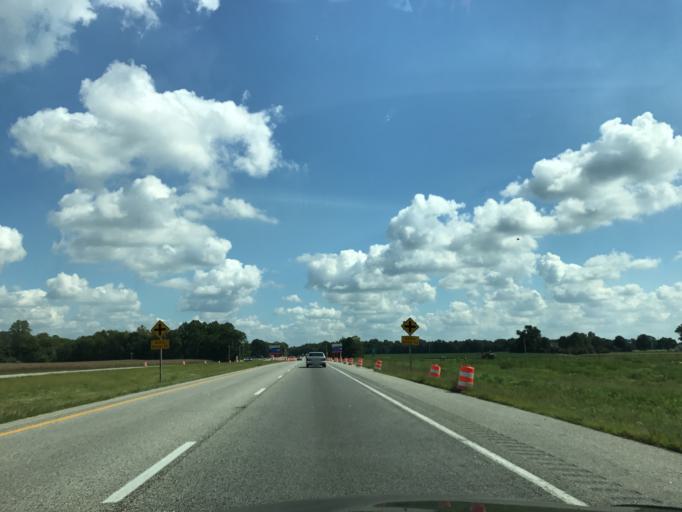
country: US
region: Maryland
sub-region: Queen Anne's County
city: Centreville
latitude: 39.0175
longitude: -76.0525
